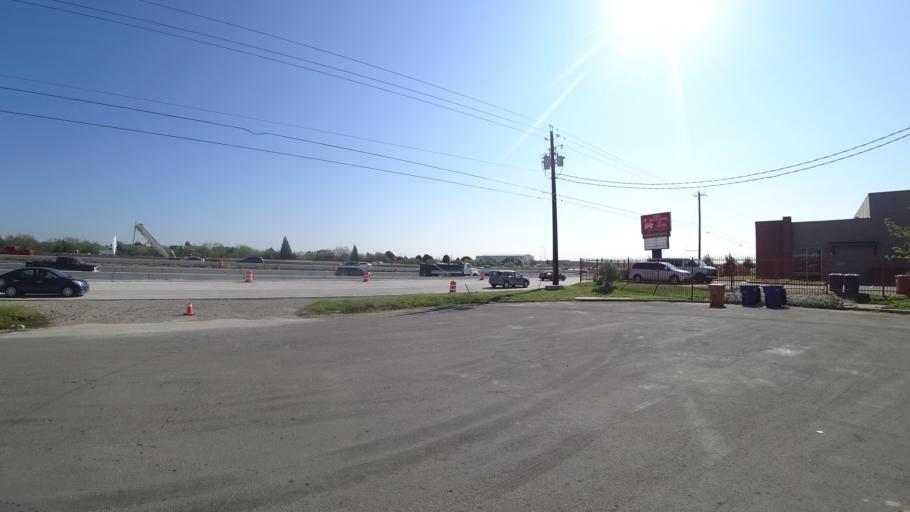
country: US
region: Texas
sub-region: Travis County
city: Austin
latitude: 30.3184
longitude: -97.6653
